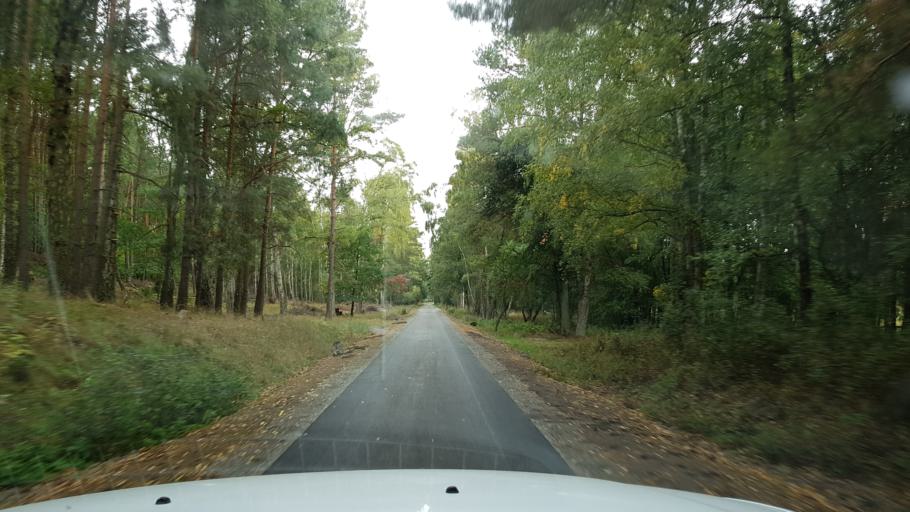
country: PL
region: West Pomeranian Voivodeship
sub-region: Powiat gryfinski
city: Cedynia
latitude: 52.8368
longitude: 14.2690
